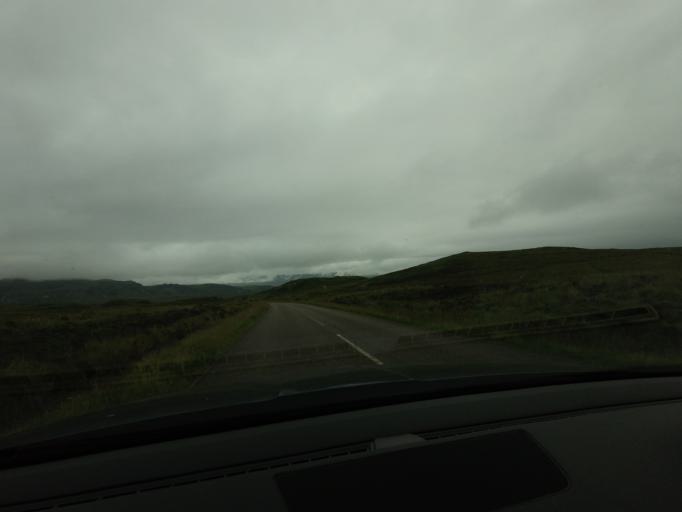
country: GB
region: Scotland
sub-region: Highland
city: Golspie
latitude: 58.5063
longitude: -4.6000
